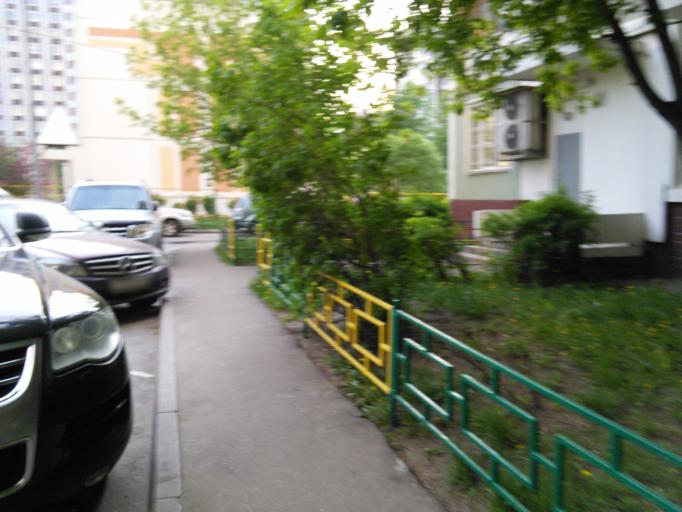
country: RU
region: Moscow
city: Mar'ina Roshcha
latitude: 55.8033
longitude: 37.6146
